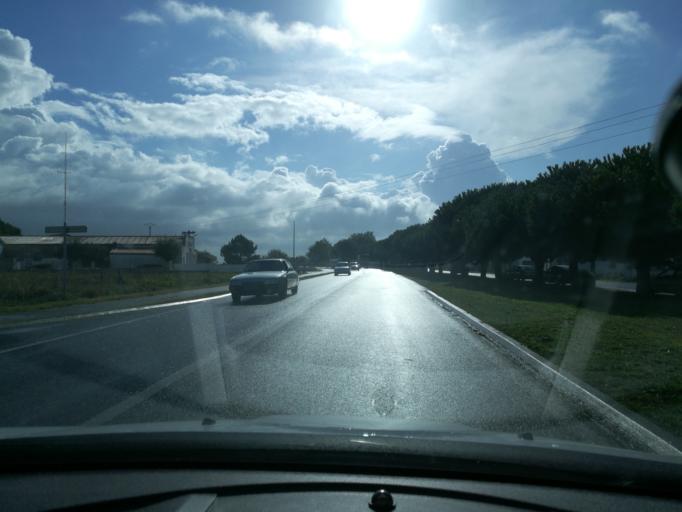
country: FR
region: Poitou-Charentes
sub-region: Departement de la Charente-Maritime
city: Sainte-Marie-de-Re
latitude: 46.1551
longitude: -1.3146
